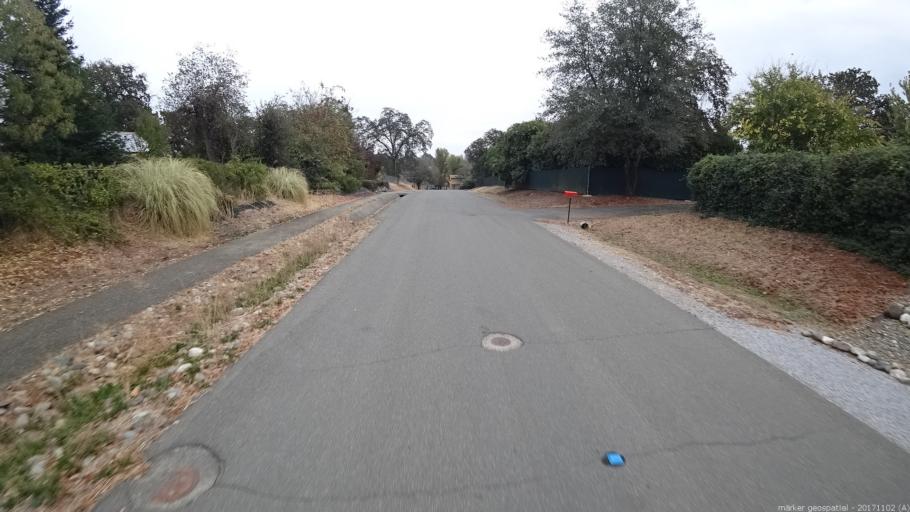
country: US
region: California
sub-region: Shasta County
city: Shasta Lake
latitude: 40.6522
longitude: -122.3181
